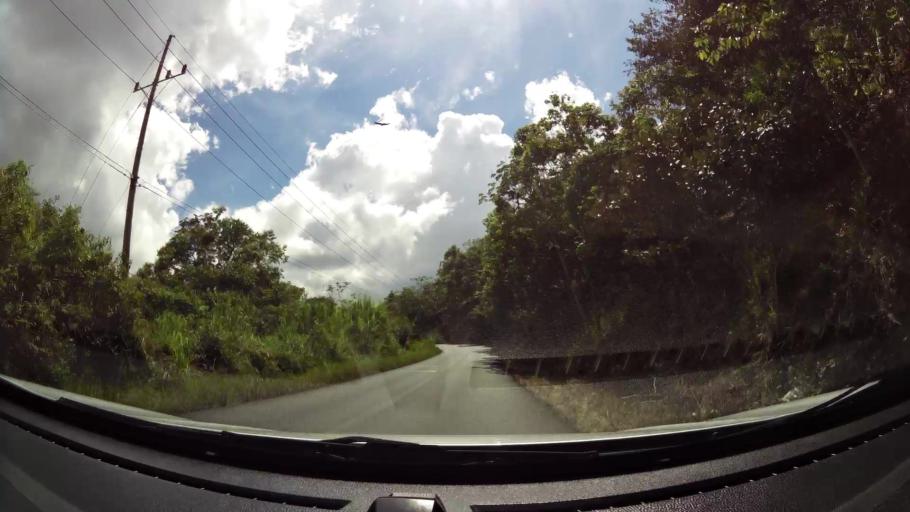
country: CR
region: San Jose
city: San Isidro
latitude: 9.3373
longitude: -83.7351
